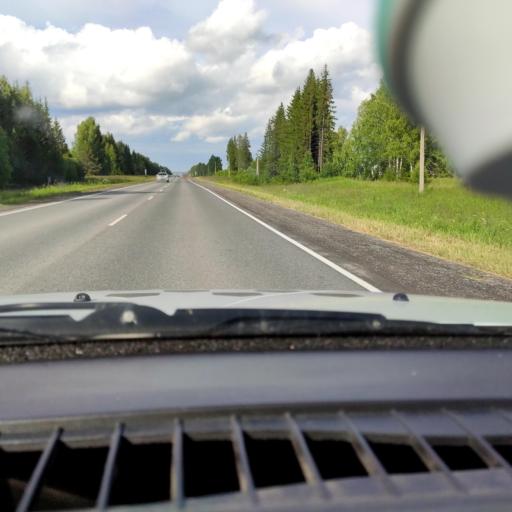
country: RU
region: Perm
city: Orda
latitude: 57.2549
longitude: 57.0041
